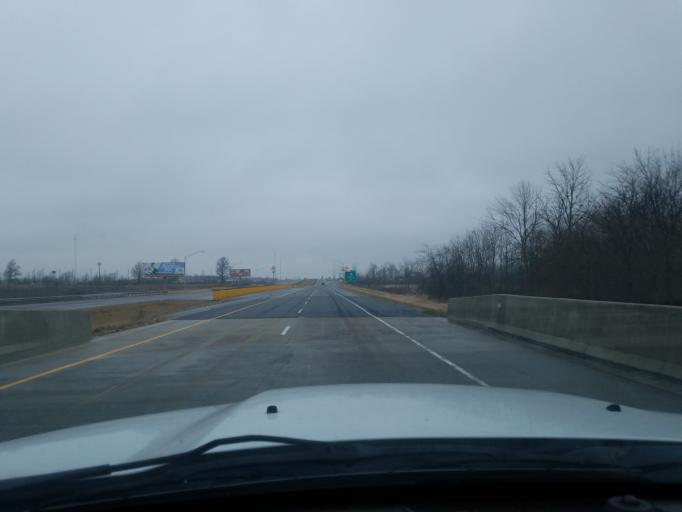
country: US
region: Indiana
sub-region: Grant County
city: Gas City
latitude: 40.5464
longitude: -85.5507
